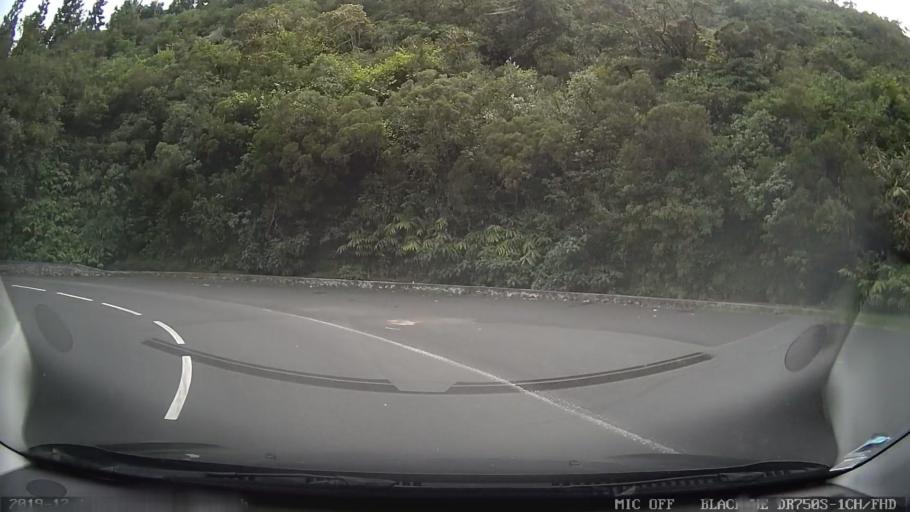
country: RE
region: Reunion
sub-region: Reunion
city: Cilaos
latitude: -21.1570
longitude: 55.6020
